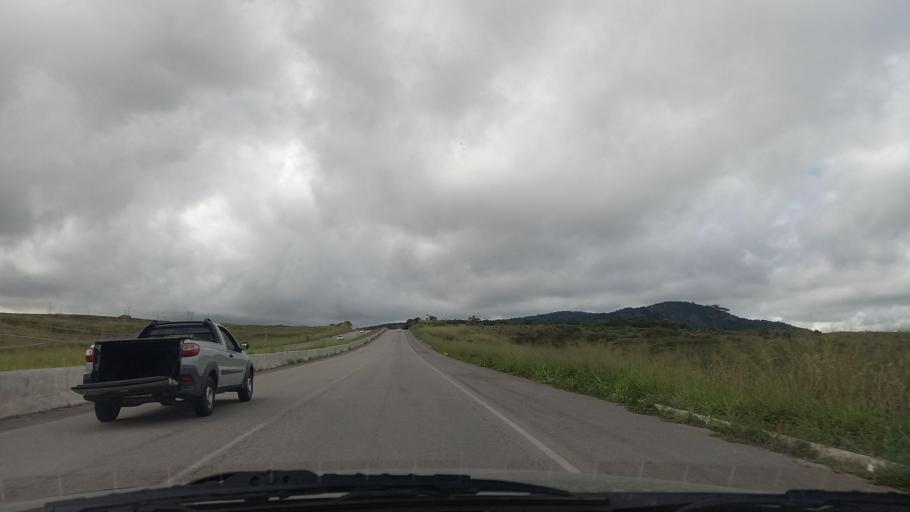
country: BR
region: Pernambuco
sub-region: Caruaru
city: Caruaru
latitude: -8.3229
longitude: -35.9895
